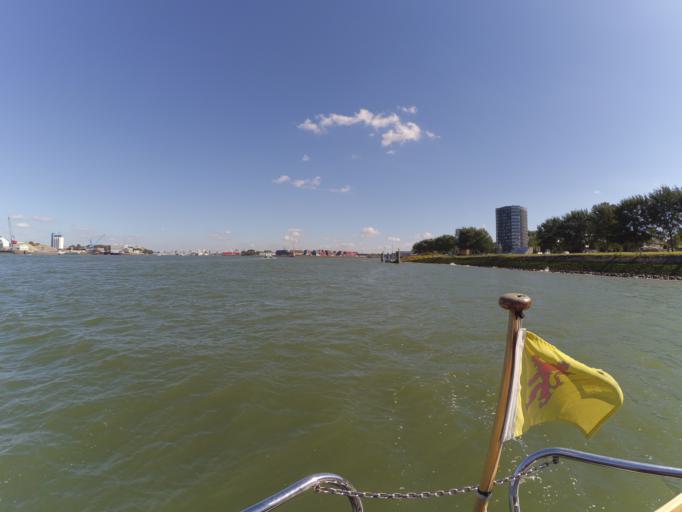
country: NL
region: South Holland
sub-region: Gemeente Schiedam
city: Schiedam
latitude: 51.8953
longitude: 4.3868
